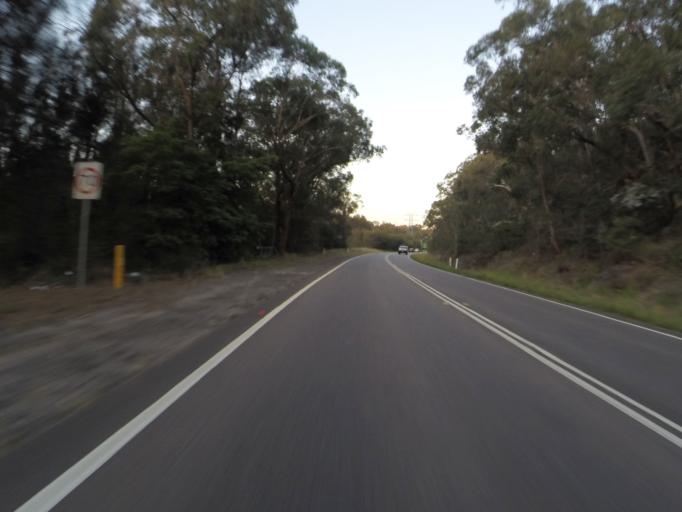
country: AU
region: New South Wales
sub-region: Bankstown
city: Padstow
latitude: -33.9704
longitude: 151.0257
